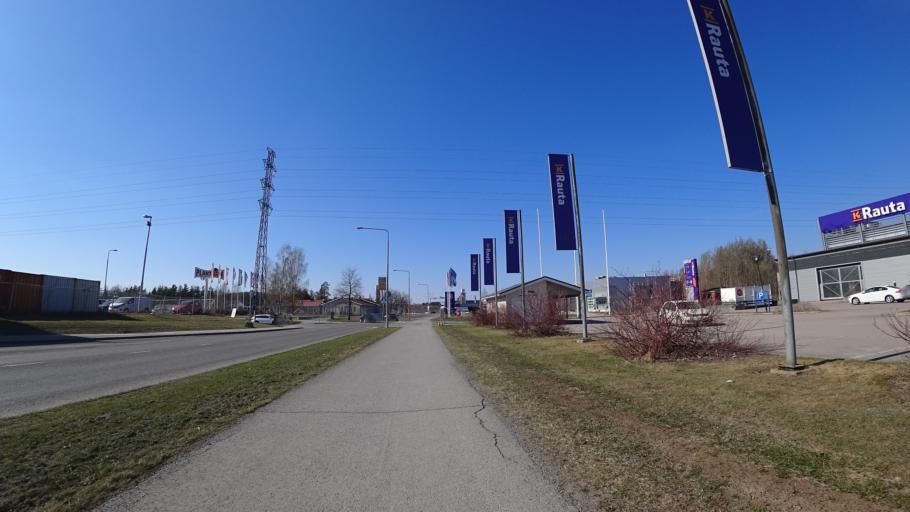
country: FI
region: Pirkanmaa
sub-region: Tampere
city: Pirkkala
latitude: 61.5203
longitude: 23.6568
